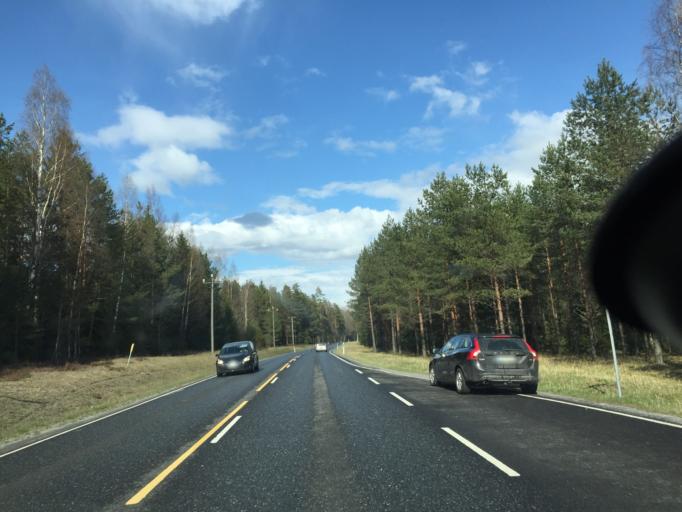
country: FI
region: Uusimaa
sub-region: Helsinki
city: Karjalohja
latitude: 60.1226
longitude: 23.8118
